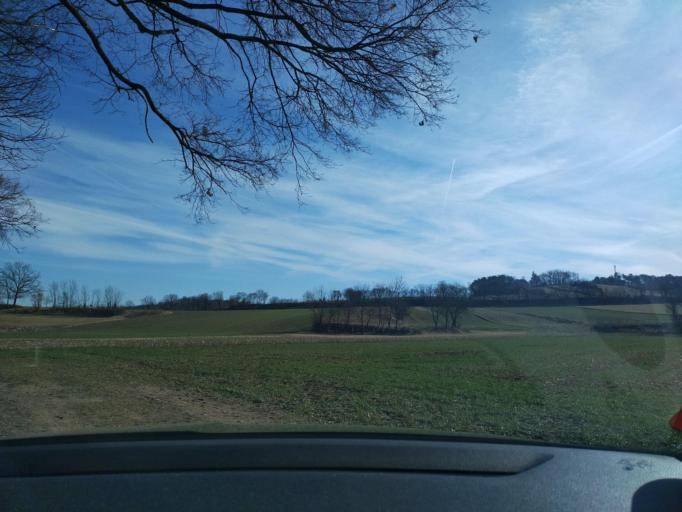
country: AT
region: Lower Austria
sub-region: Politischer Bezirk Neunkirchen
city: Pitten
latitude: 47.7294
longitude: 16.1754
